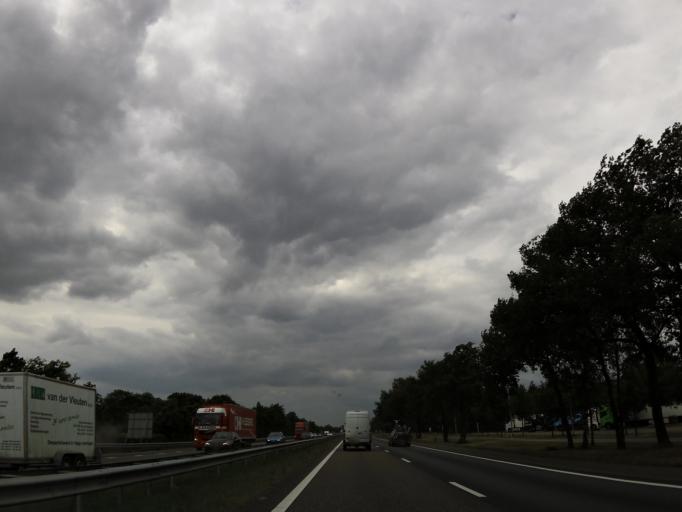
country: NL
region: North Brabant
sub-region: Gemeente Cranendonck
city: Cranendonck
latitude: 51.3251
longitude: 5.5912
